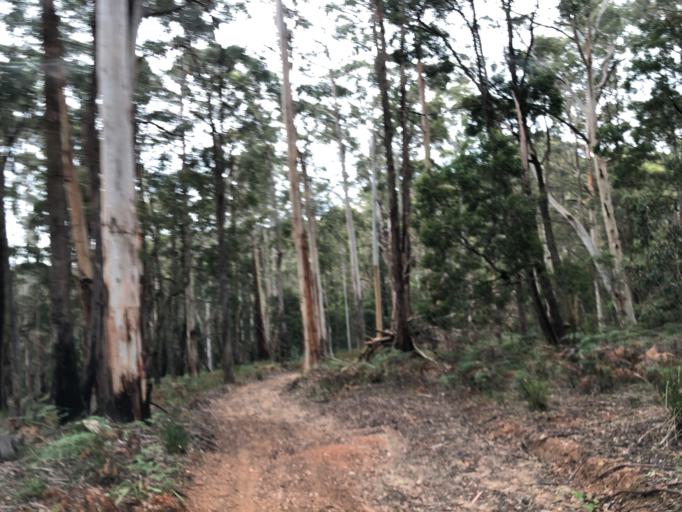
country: AU
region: Victoria
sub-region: Moorabool
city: Bacchus Marsh
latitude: -37.4408
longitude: 144.3301
